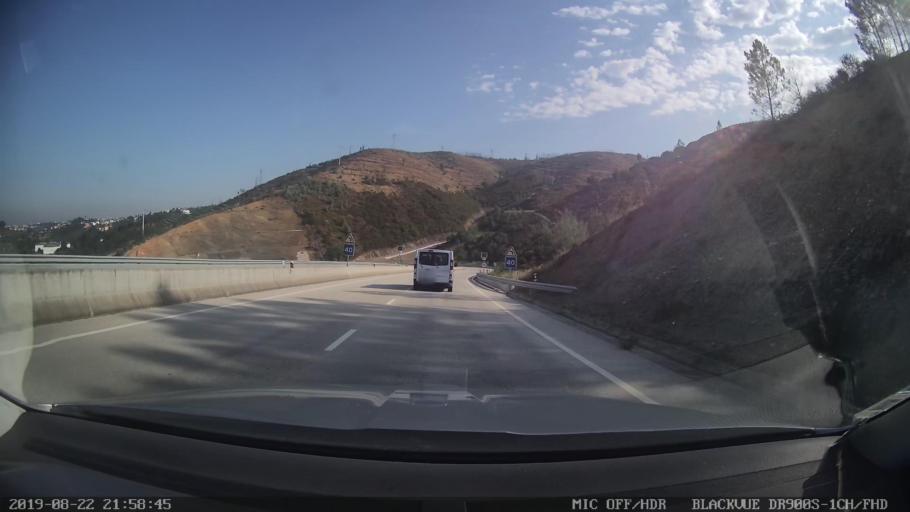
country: PT
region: Coimbra
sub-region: Coimbra
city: Coimbra
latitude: 40.1792
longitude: -8.3888
